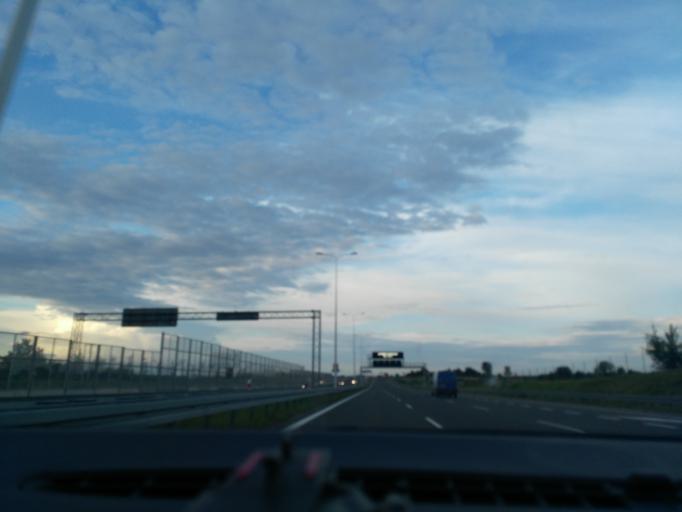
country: PL
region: Lublin Voivodeship
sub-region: Powiat lubelski
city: Jastkow
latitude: 51.2914
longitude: 22.4664
